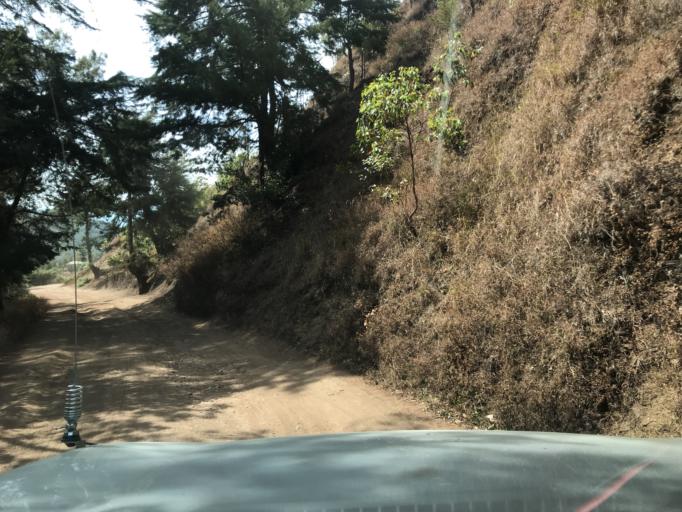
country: TL
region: Ainaro
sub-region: Ainaro
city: Ainaro
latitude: -8.8910
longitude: 125.5175
